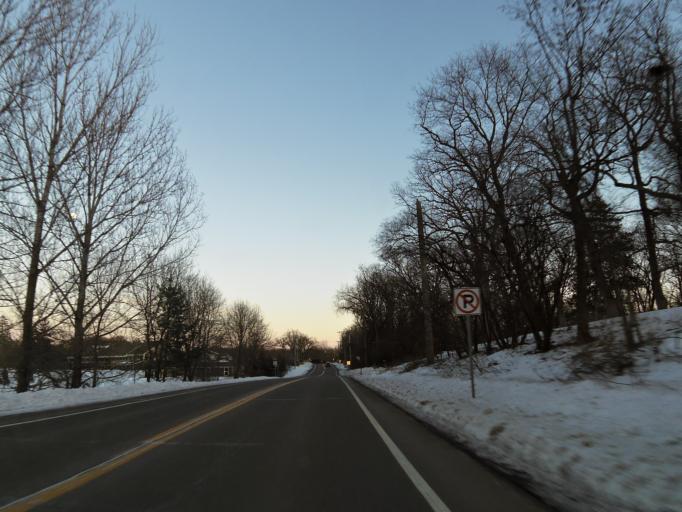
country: US
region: Minnesota
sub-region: Washington County
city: Dellwood
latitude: 45.0968
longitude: -92.9792
